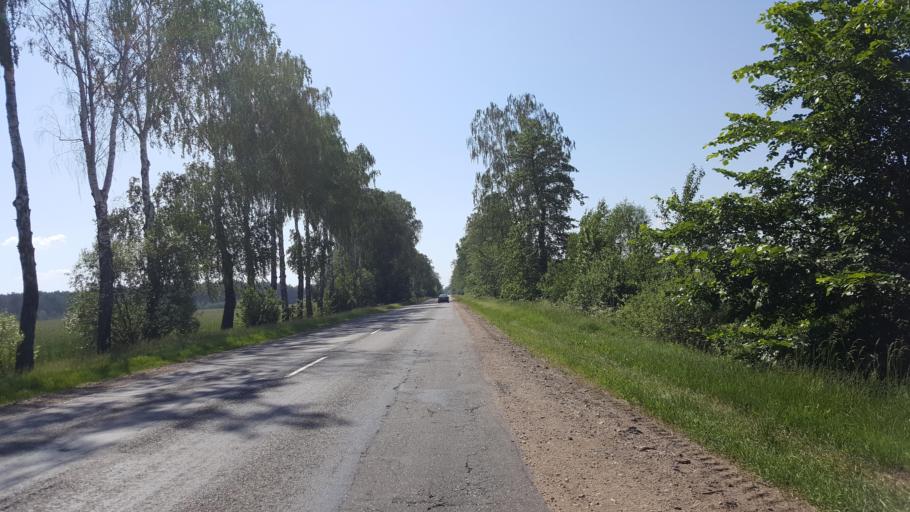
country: BY
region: Brest
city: Zhabinka
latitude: 52.2474
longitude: 23.9721
